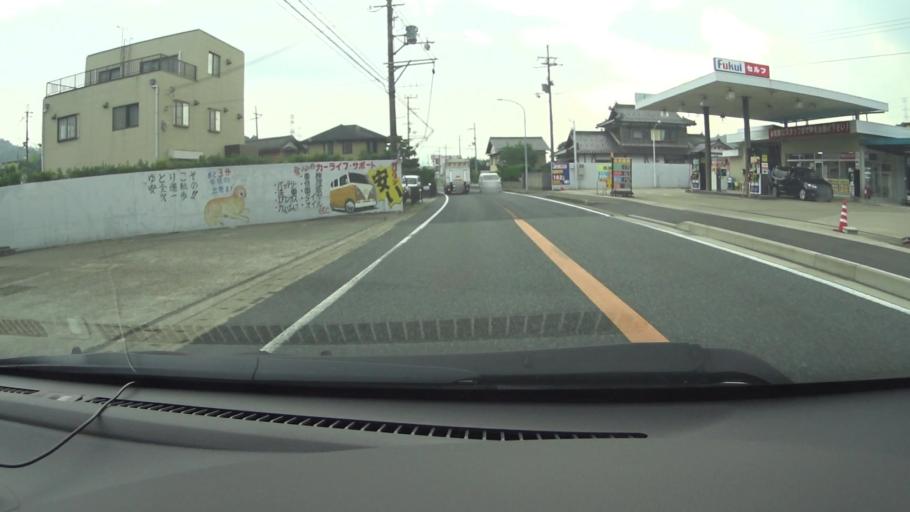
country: JP
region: Kyoto
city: Ayabe
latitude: 35.3263
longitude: 135.2926
